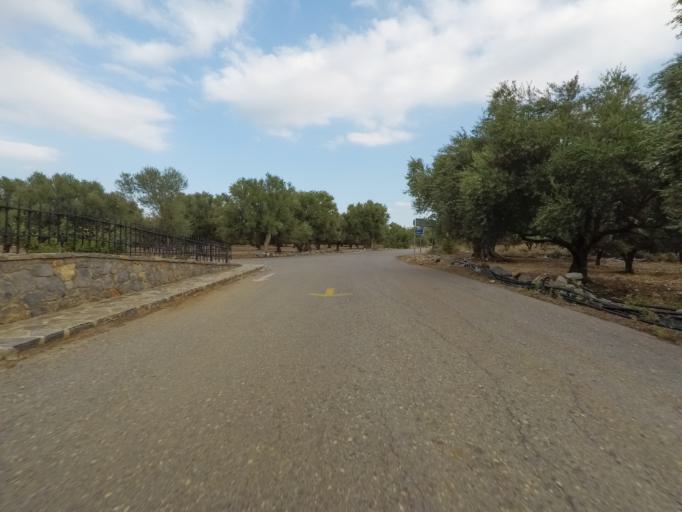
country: GR
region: Crete
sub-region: Nomos Lasithiou
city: Kritsa
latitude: 35.1740
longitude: 25.6533
